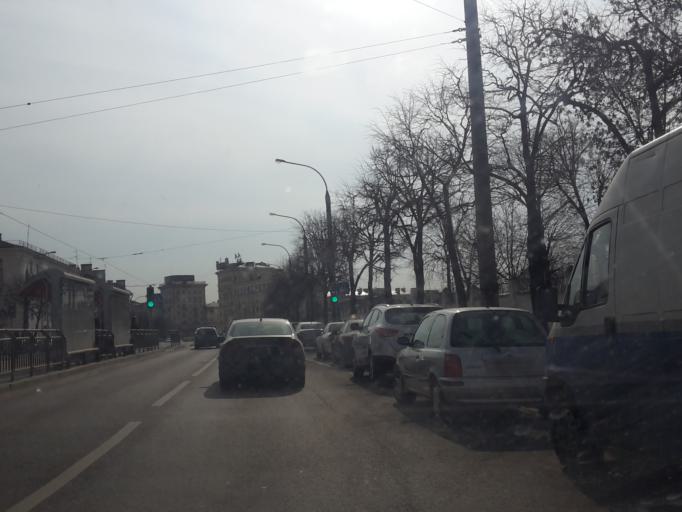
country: BY
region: Minsk
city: Minsk
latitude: 53.9131
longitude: 27.5750
